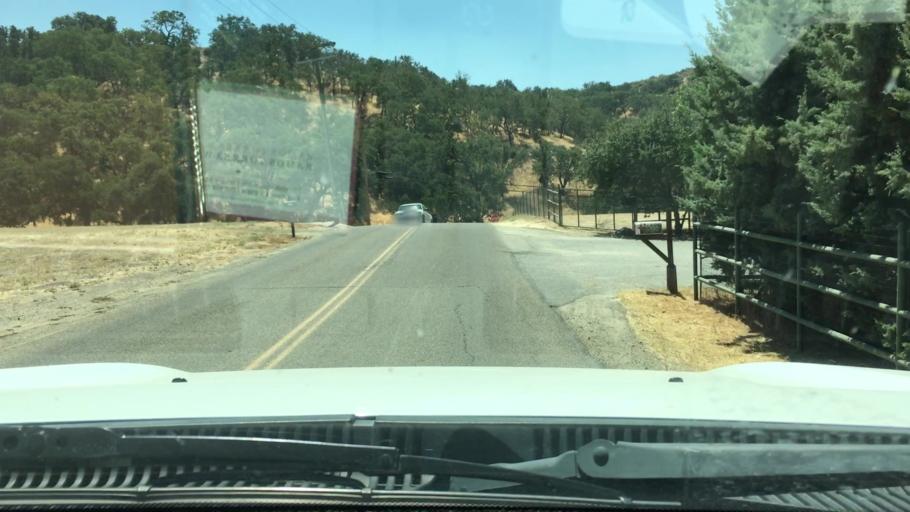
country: US
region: California
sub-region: San Luis Obispo County
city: Atascadero
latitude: 35.5114
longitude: -120.6385
